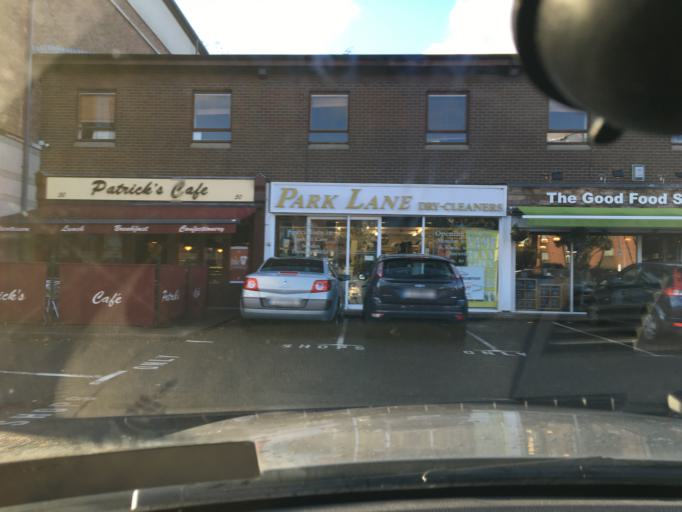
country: IE
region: Leinster
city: Ringsend
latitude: 53.3304
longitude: -6.2248
